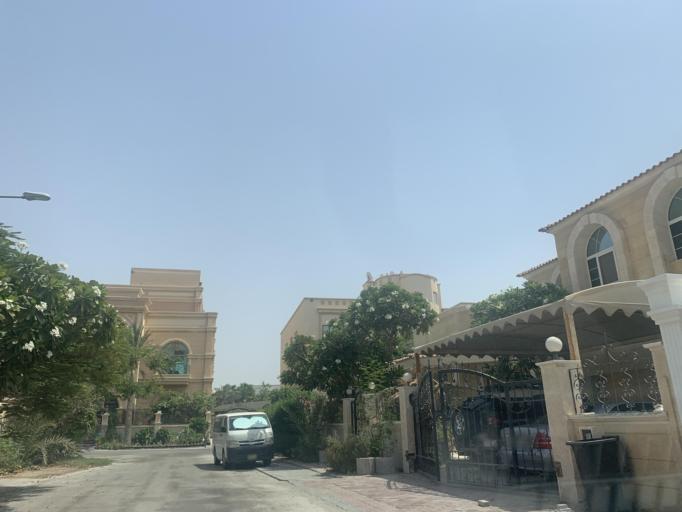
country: BH
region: Manama
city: Jidd Hafs
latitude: 26.1987
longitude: 50.5040
